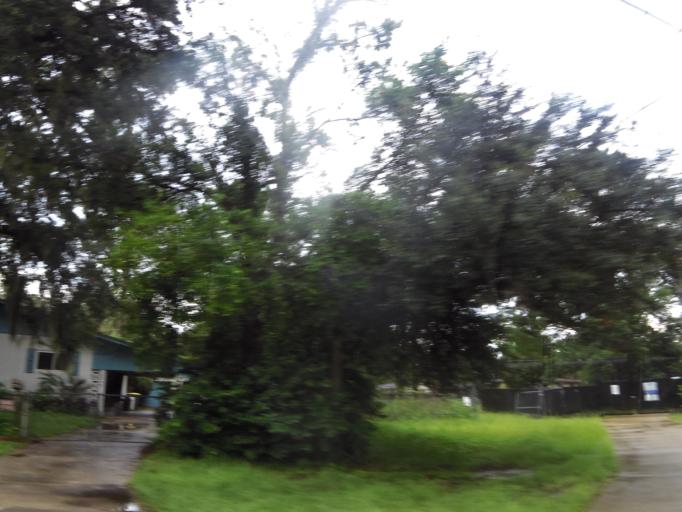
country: US
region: Florida
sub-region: Duval County
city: Jacksonville
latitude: 30.2857
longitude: -81.5962
